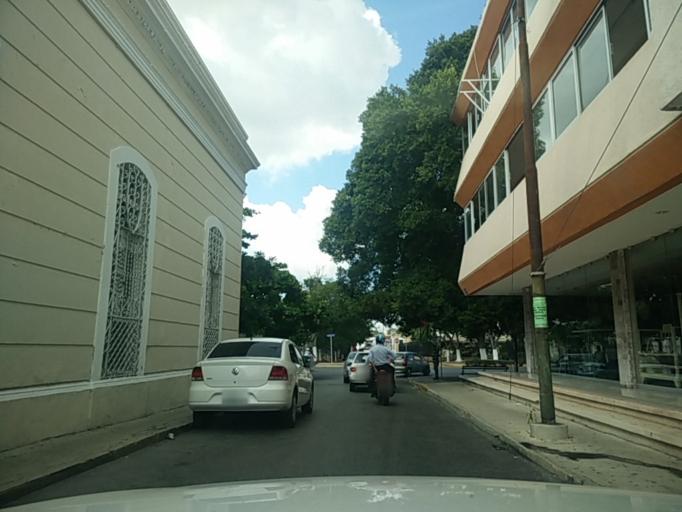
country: MX
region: Yucatan
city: Merida
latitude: 20.9763
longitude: -89.6189
